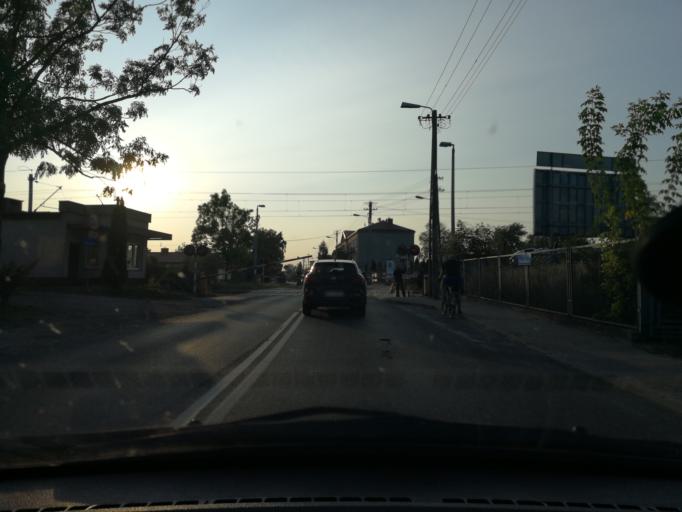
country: PL
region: Lodz Voivodeship
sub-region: Skierniewice
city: Skierniewice
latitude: 51.9611
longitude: 20.1355
